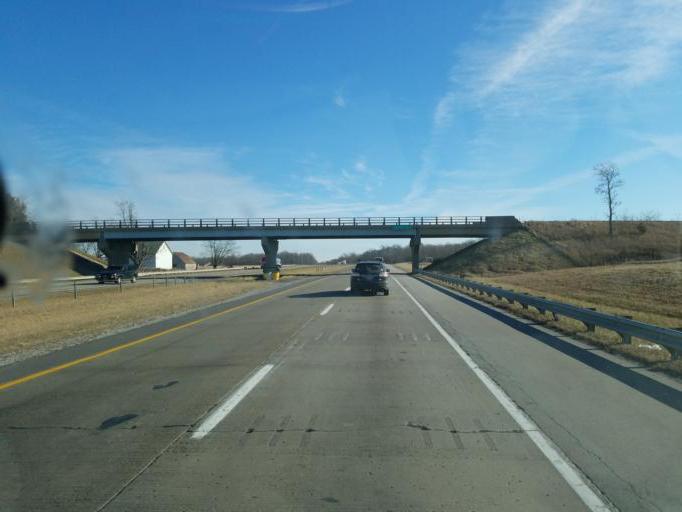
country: US
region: Indiana
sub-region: Henry County
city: Knightstown
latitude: 39.8446
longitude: -85.5166
